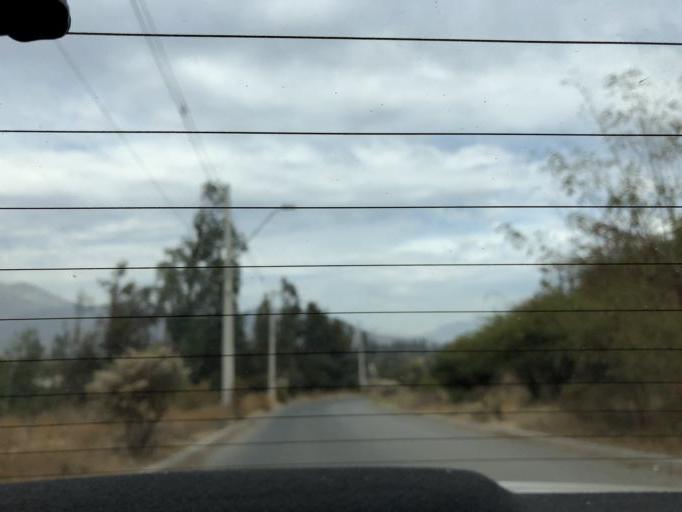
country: CL
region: Santiago Metropolitan
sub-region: Provincia de Cordillera
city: Puente Alto
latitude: -33.5920
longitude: -70.5196
